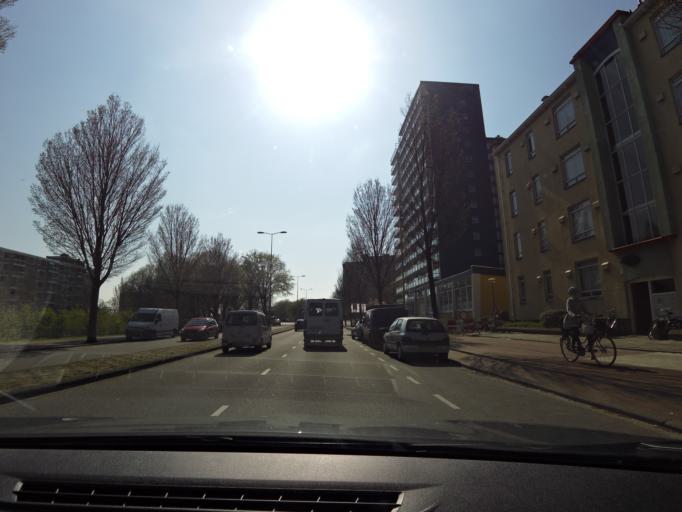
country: NL
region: South Holland
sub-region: Gemeente Den Haag
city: The Hague
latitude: 52.0516
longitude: 4.3013
